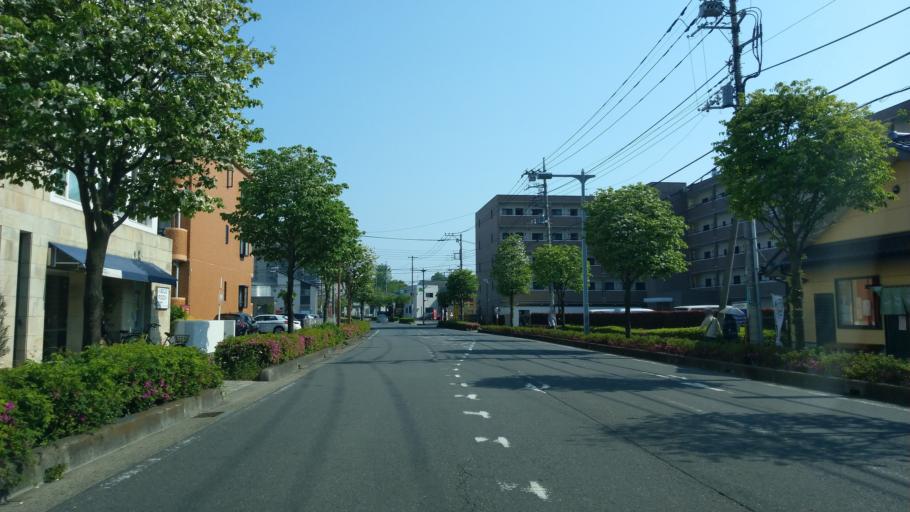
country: JP
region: Saitama
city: Oi
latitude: 35.8588
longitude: 139.5192
